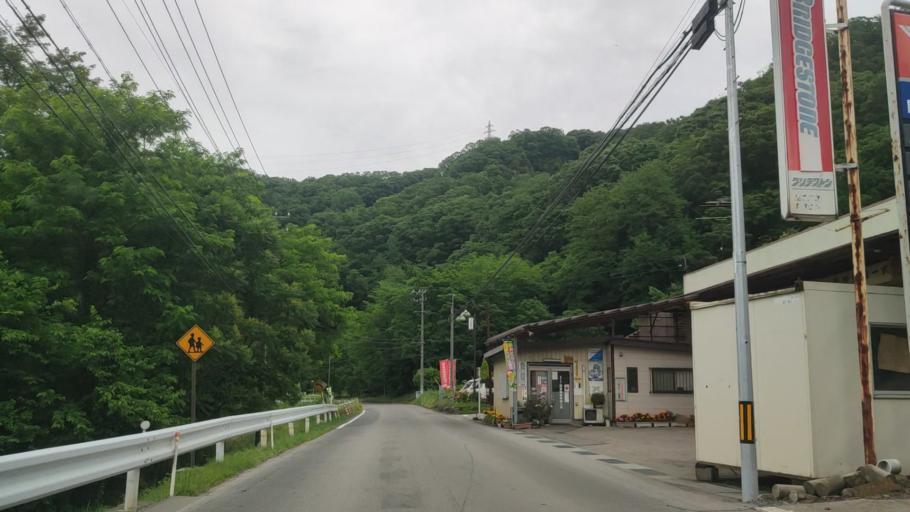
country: JP
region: Nagano
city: Kamimaruko
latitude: 36.3321
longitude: 138.3503
